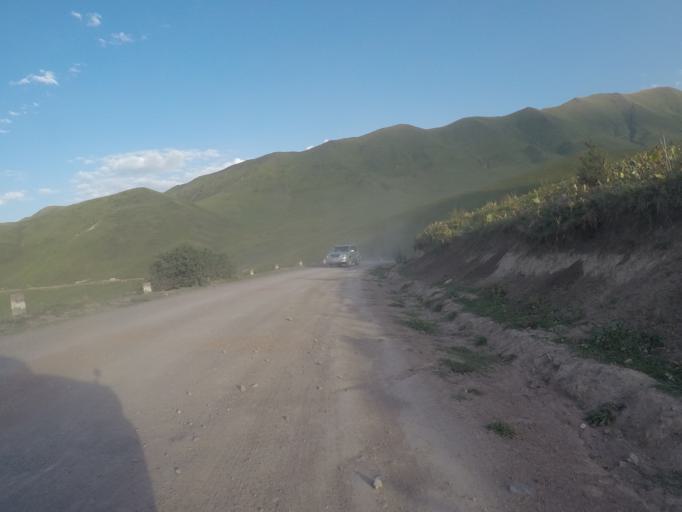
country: KG
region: Chuy
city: Bishkek
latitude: 42.6412
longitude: 74.6346
